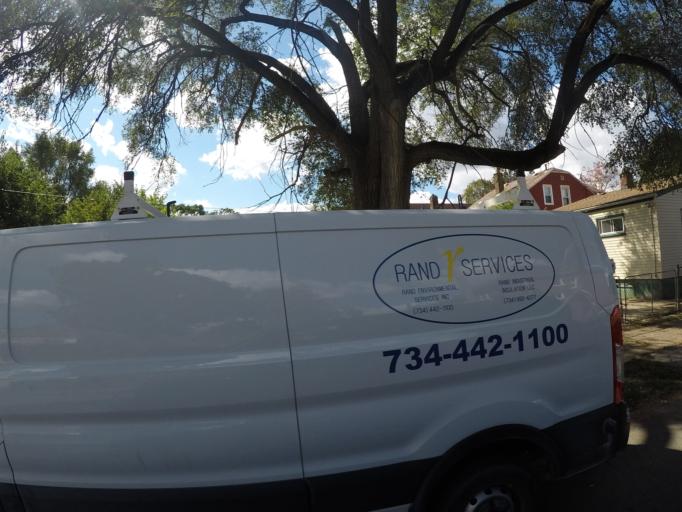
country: US
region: Michigan
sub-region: Wayne County
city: Lincoln Park
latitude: 42.2598
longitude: -83.1640
